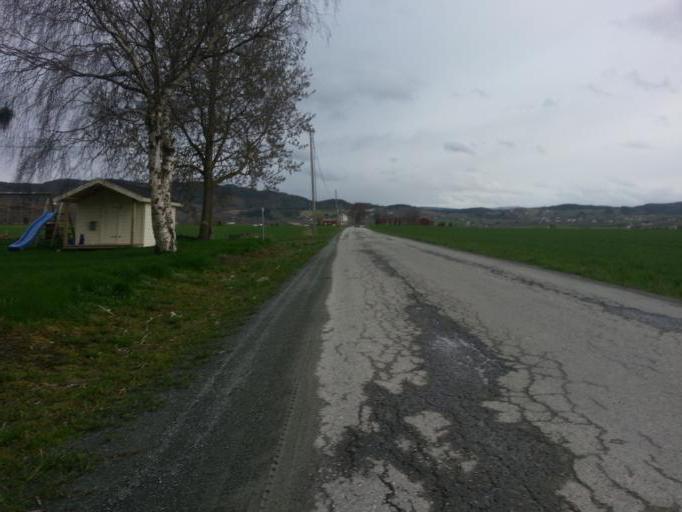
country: NO
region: Nord-Trondelag
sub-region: Levanger
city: Skogn
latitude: 63.6948
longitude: 11.2007
